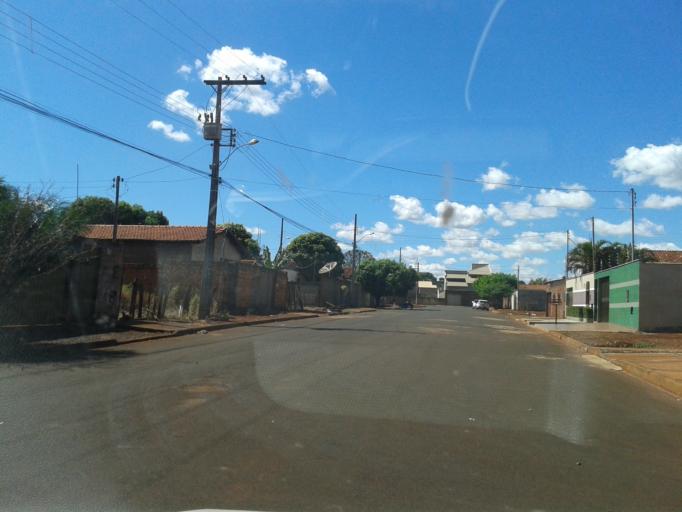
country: BR
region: Minas Gerais
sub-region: Centralina
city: Centralina
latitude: -18.5937
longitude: -49.1994
